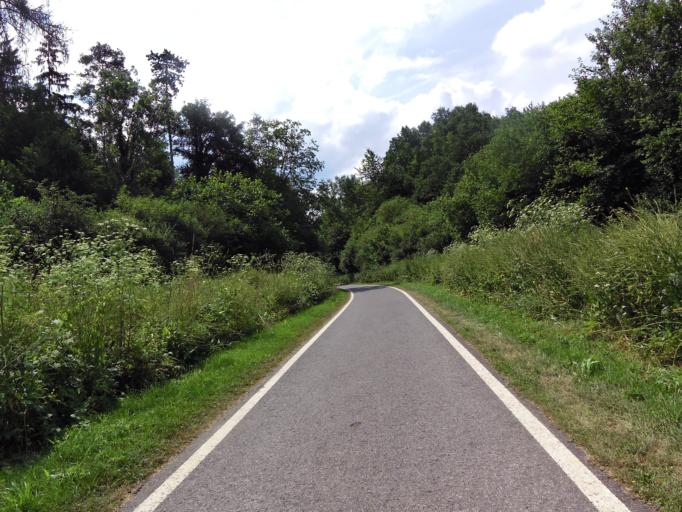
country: DE
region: Bavaria
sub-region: Regierungsbezirk Unterfranken
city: Reichenberg
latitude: 49.7435
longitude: 9.9483
